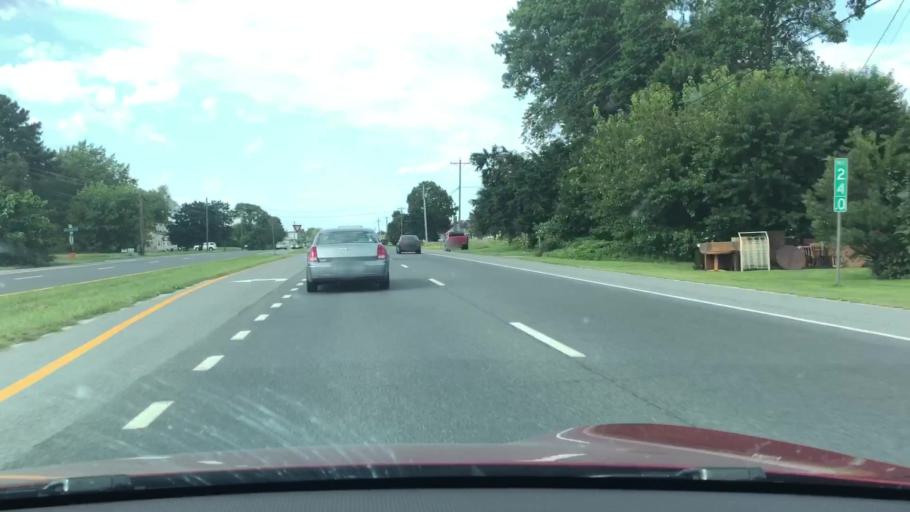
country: US
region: Delaware
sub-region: Sussex County
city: Bridgeville
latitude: 38.7947
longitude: -75.5910
